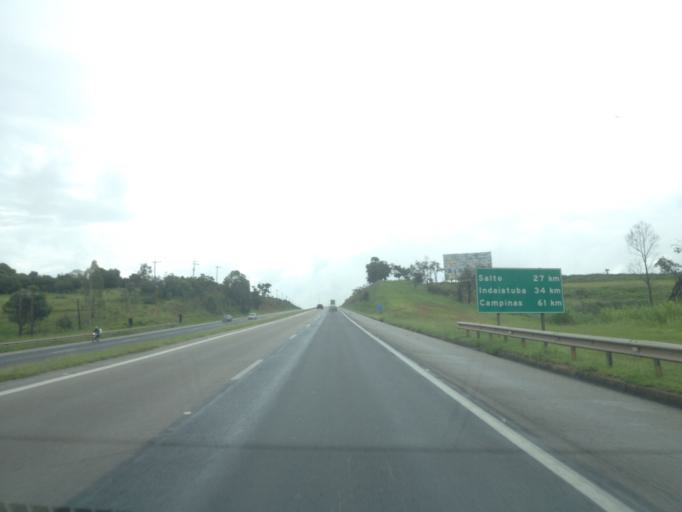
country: BR
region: Sao Paulo
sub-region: Itu
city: Itu
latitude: -23.3565
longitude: -47.3256
